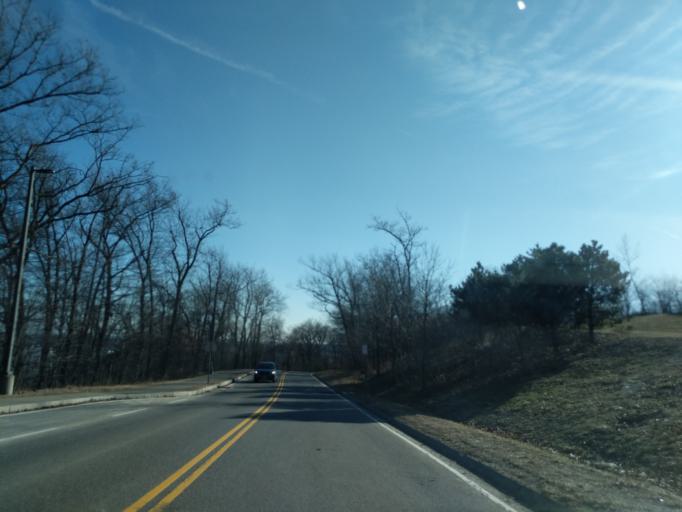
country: US
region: Massachusetts
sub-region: Worcester County
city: Hamilton
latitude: 42.2774
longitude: -71.7796
